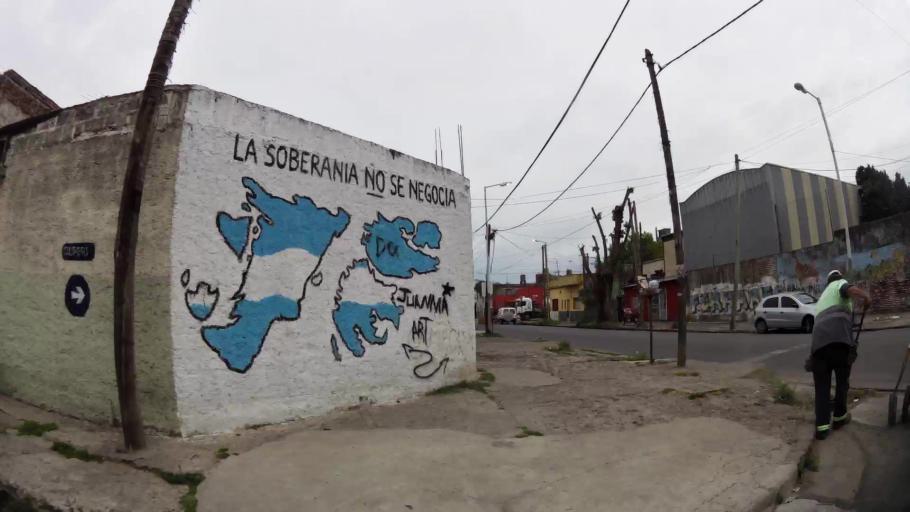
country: AR
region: Buenos Aires
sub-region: Partido de Avellaneda
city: Avellaneda
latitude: -34.6542
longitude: -58.3472
